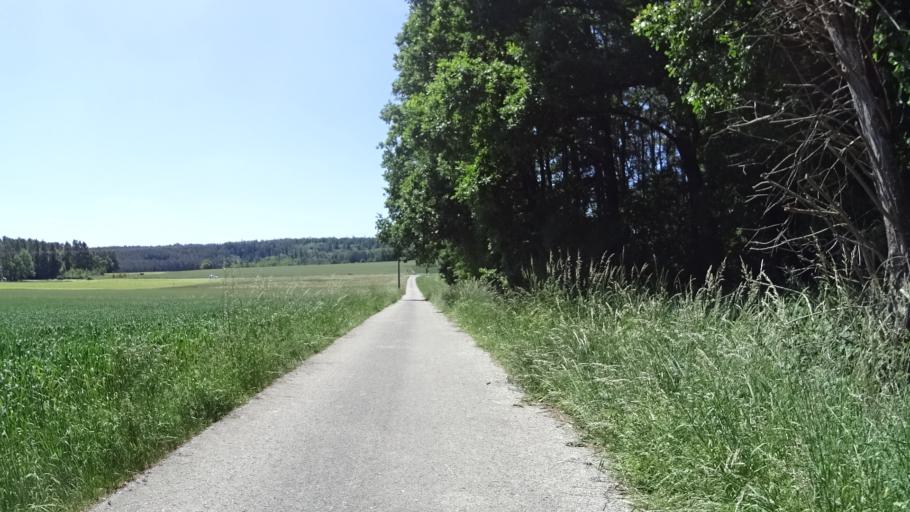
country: DE
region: Bavaria
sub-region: Regierungsbezirk Mittelfranken
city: Absberg
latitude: 49.1123
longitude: 10.9007
